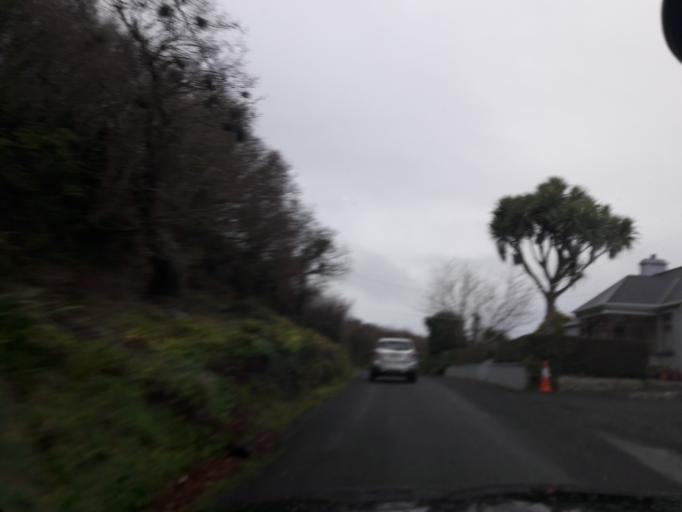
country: IE
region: Ulster
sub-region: County Donegal
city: Buncrana
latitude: 55.2327
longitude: -7.6175
